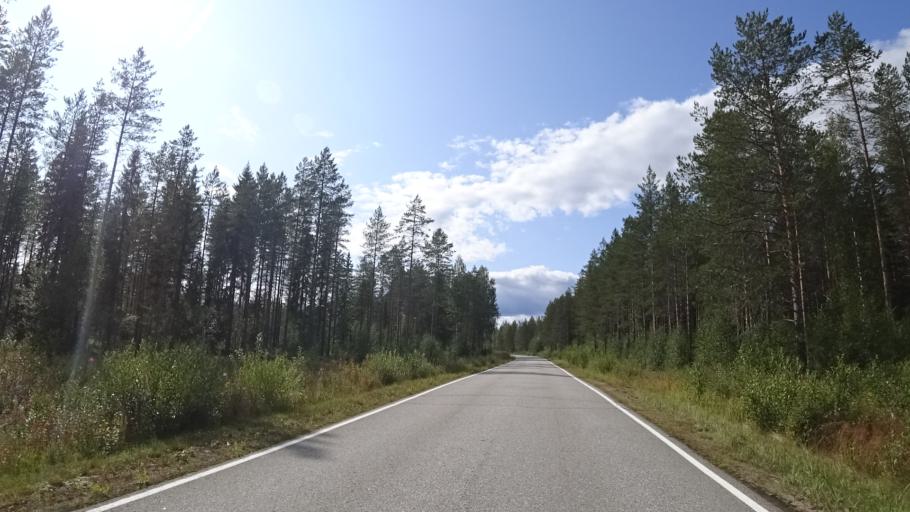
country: FI
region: North Karelia
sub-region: Joensuu
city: Ilomantsi
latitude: 62.4126
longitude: 30.9893
